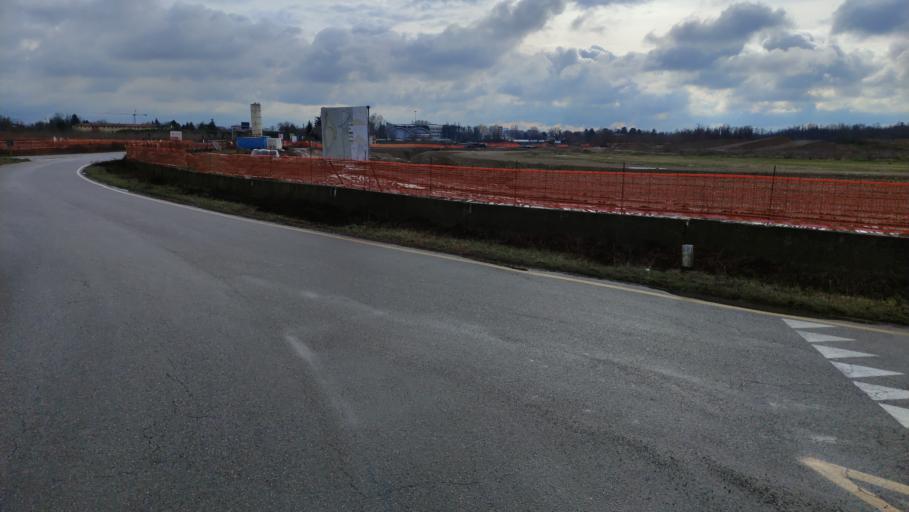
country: IT
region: Lombardy
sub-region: Citta metropolitana di Milano
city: Senago
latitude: 45.5640
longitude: 9.1160
